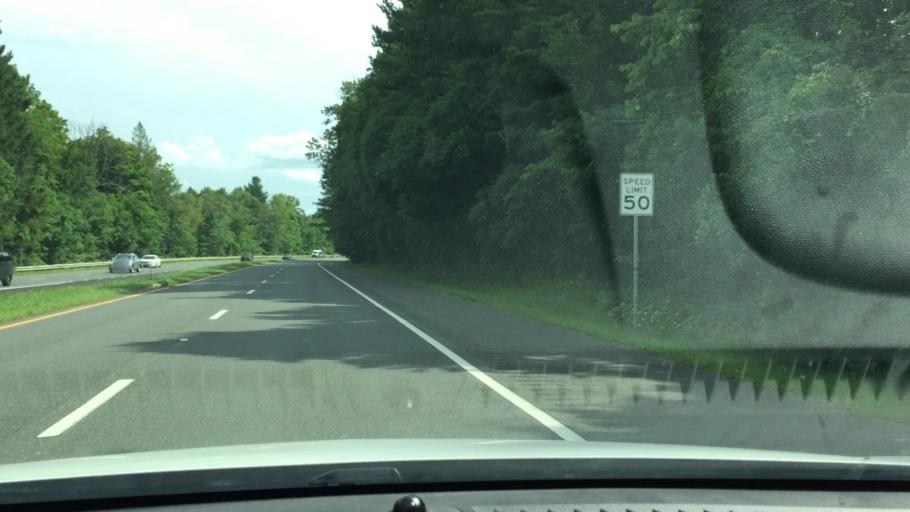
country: US
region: Massachusetts
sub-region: Berkshire County
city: Lenox
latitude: 42.3548
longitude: -73.2686
